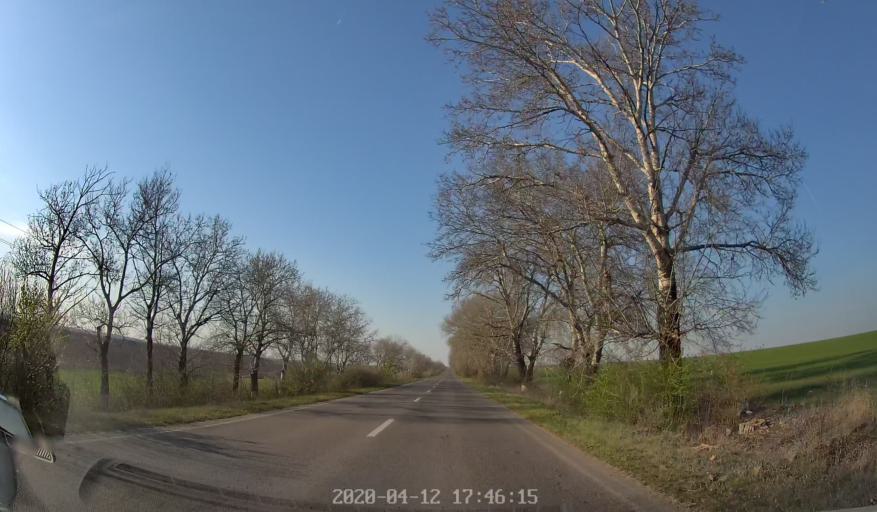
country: MD
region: Telenesti
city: Cocieri
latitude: 47.3662
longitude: 29.1136
